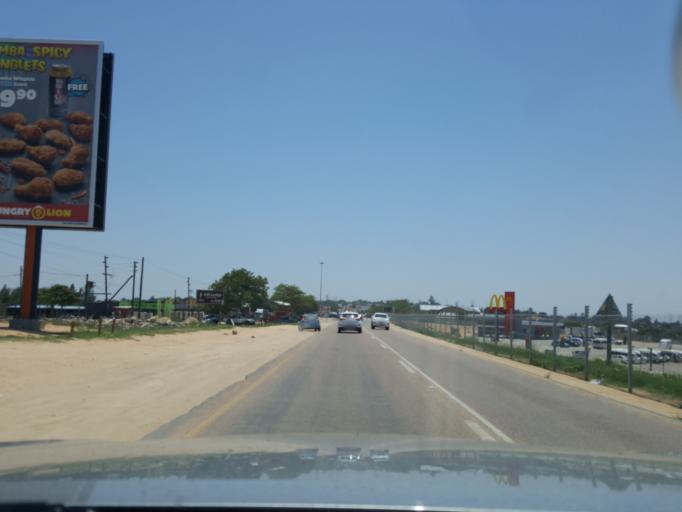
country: ZA
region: Limpopo
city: Thulamahashi
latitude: -24.6044
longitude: 31.0402
